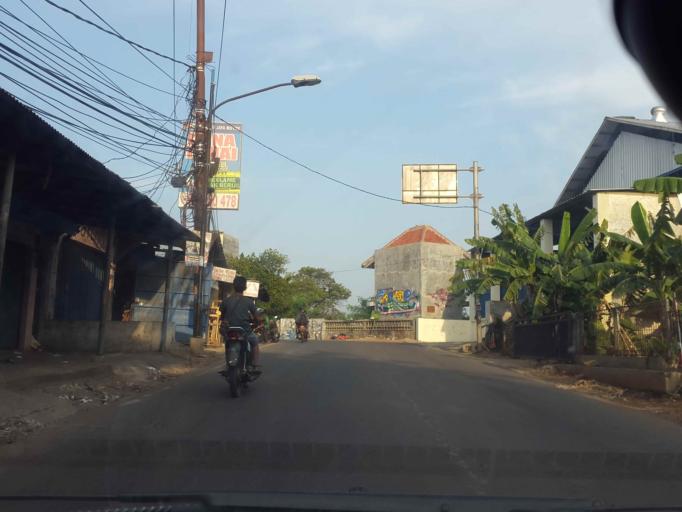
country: ID
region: Banten
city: South Tangerang
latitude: -6.2638
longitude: 106.7177
